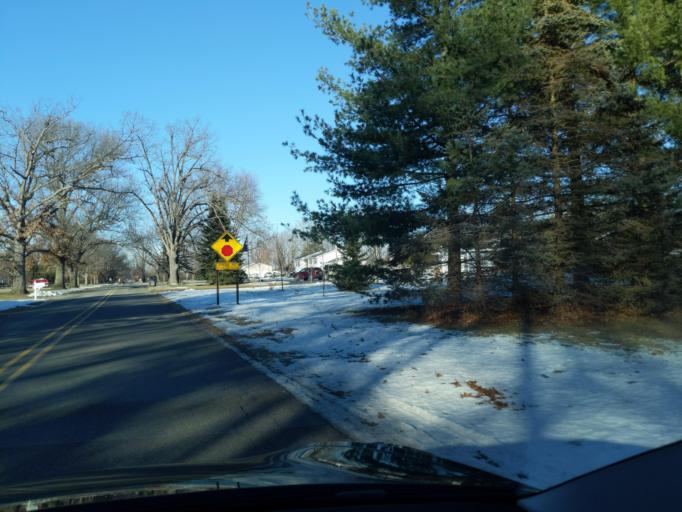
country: US
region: Michigan
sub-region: Ingham County
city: Stockbridge
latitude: 42.4372
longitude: -84.1505
